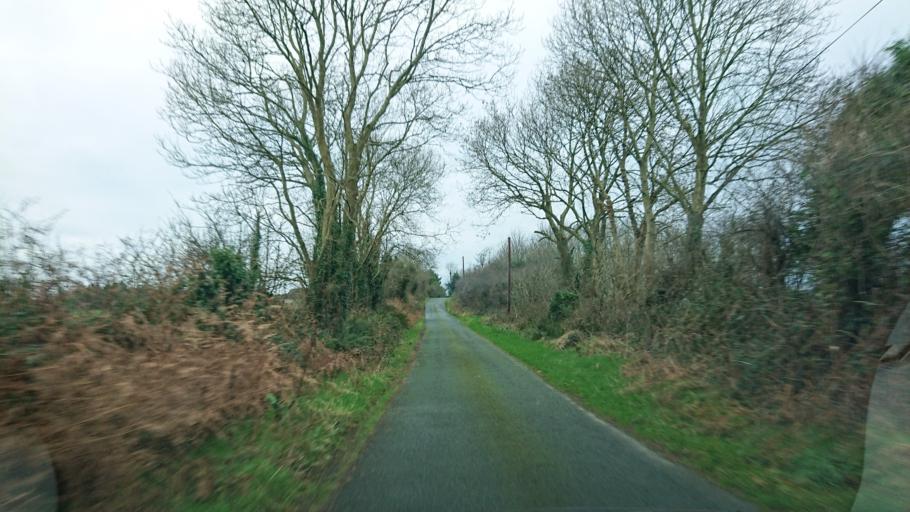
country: IE
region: Leinster
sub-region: Kilkenny
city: Mooncoin
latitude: 52.2268
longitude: -7.2615
